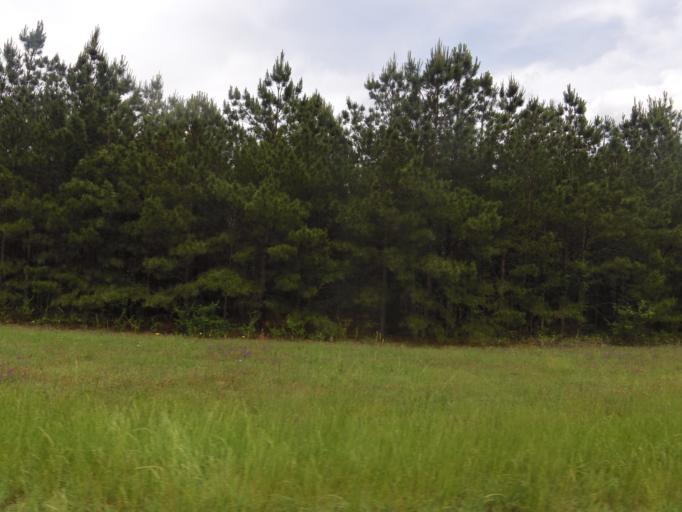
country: US
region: Georgia
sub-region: Jefferson County
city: Wrens
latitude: 33.2256
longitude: -82.4028
